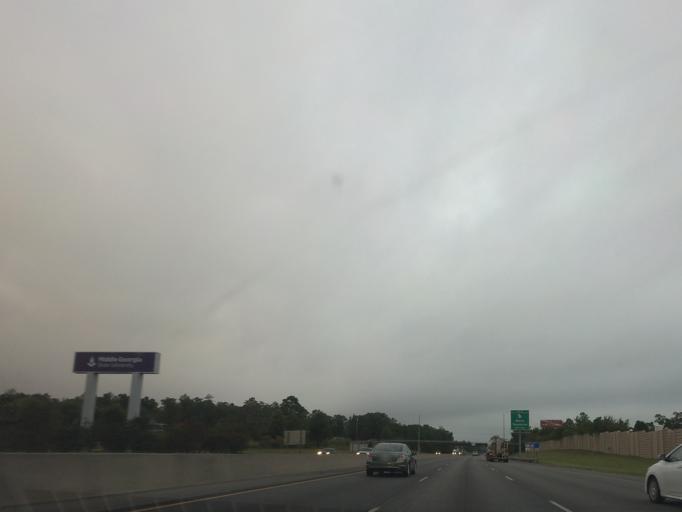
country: US
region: Georgia
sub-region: Bibb County
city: West Point
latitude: 32.8158
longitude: -83.7284
